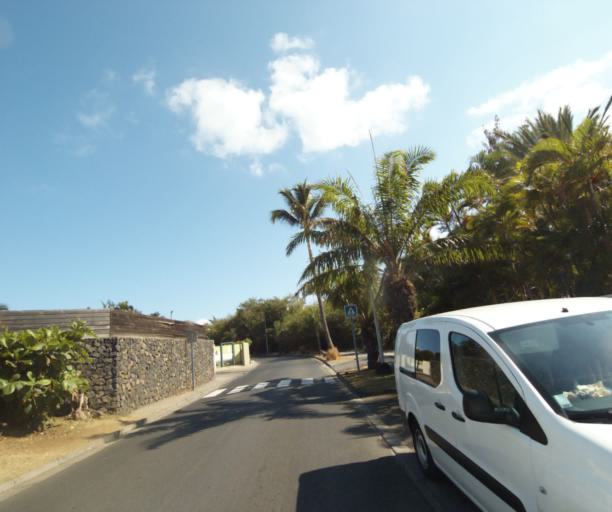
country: RE
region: Reunion
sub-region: Reunion
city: Saint-Paul
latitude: -21.0666
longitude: 55.2228
